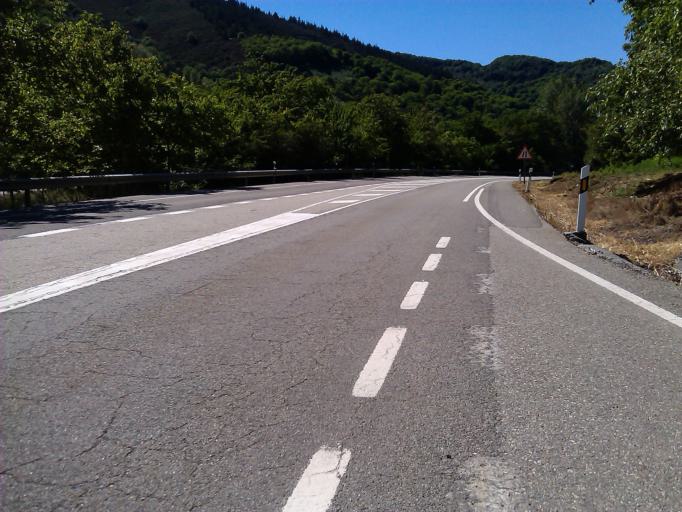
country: ES
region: Castille and Leon
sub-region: Provincia de Leon
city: Villafranca del Bierzo
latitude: 42.6254
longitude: -6.8443
